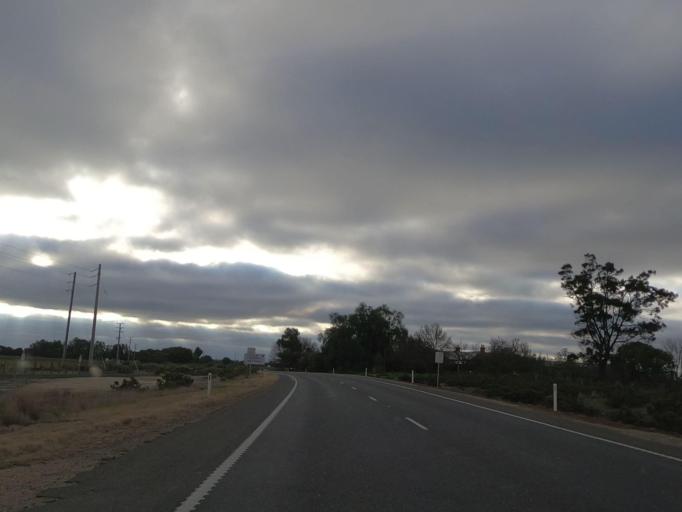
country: AU
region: Victoria
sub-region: Swan Hill
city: Swan Hill
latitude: -35.7247
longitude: 143.8900
